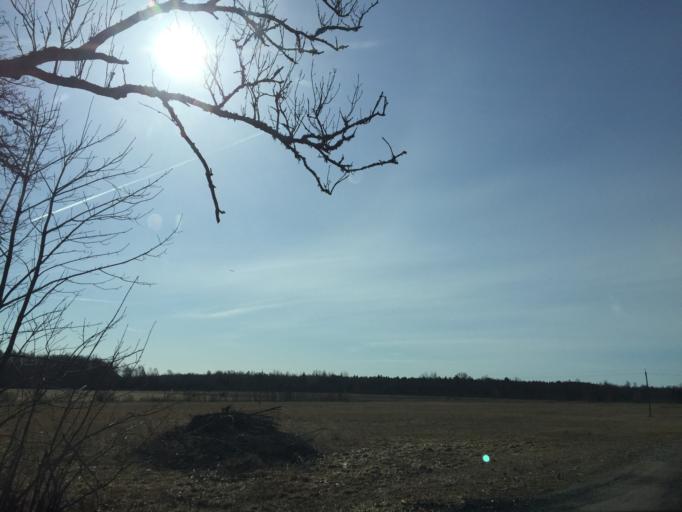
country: EE
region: Laeaene
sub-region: Ridala Parish
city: Uuemoisa
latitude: 58.6746
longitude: 23.5476
